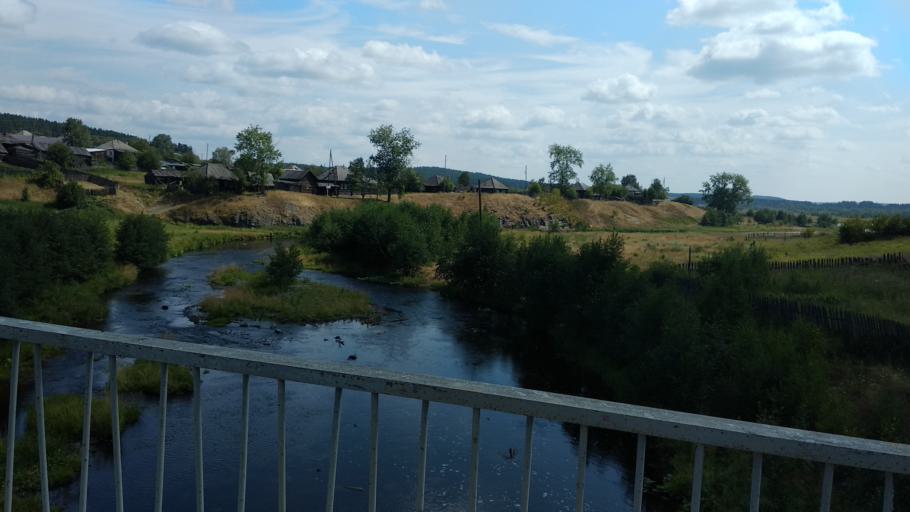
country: RU
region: Sverdlovsk
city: Valerianovsk
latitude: 59.2512
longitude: 59.5021
